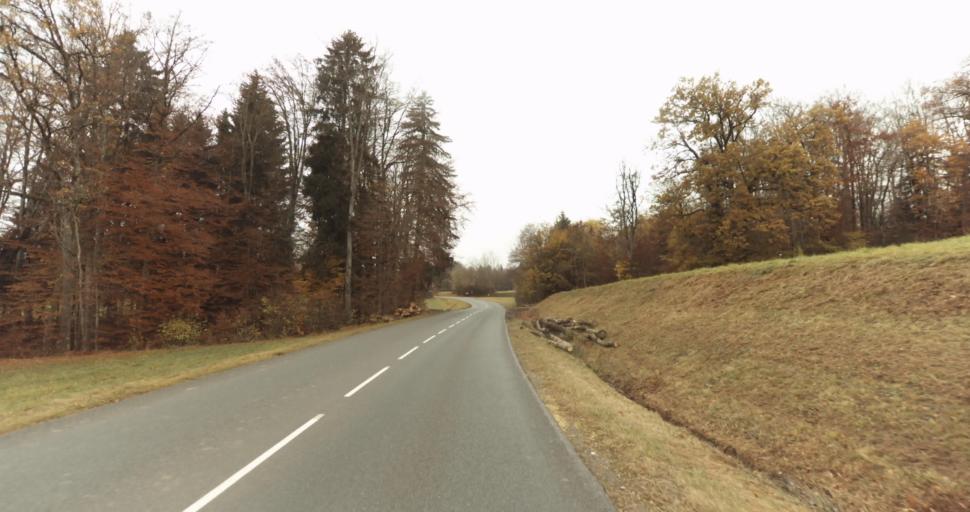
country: FR
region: Rhone-Alpes
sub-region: Departement de la Haute-Savoie
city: Evires
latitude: 46.0518
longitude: 6.2345
